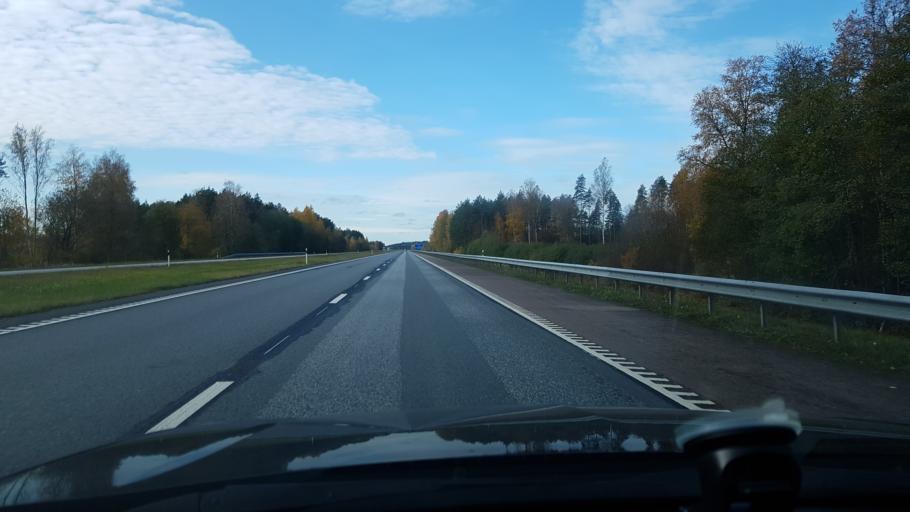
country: EE
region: Harju
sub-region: Kuusalu vald
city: Kuusalu
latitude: 59.4577
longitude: 25.5426
